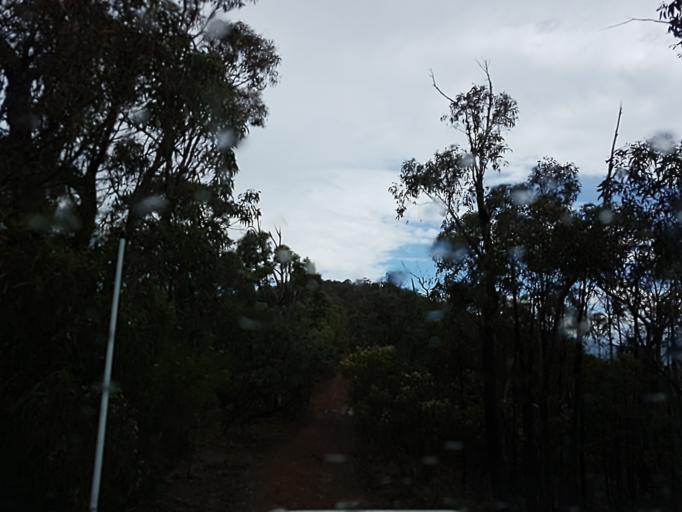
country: AU
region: New South Wales
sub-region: Snowy River
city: Jindabyne
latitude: -36.9059
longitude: 148.3410
